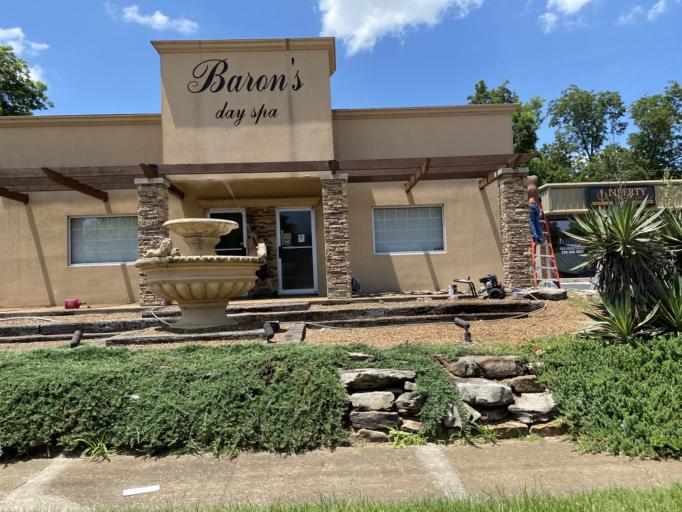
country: US
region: Alabama
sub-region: Morgan County
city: Decatur
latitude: 34.5941
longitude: -86.9804
